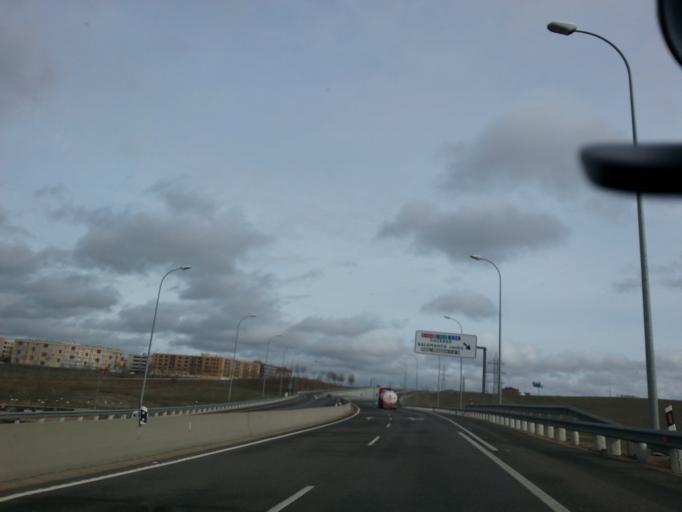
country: ES
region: Castille and Leon
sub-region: Provincia de Salamanca
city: Aldeatejada
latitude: 40.9398
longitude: -5.6755
